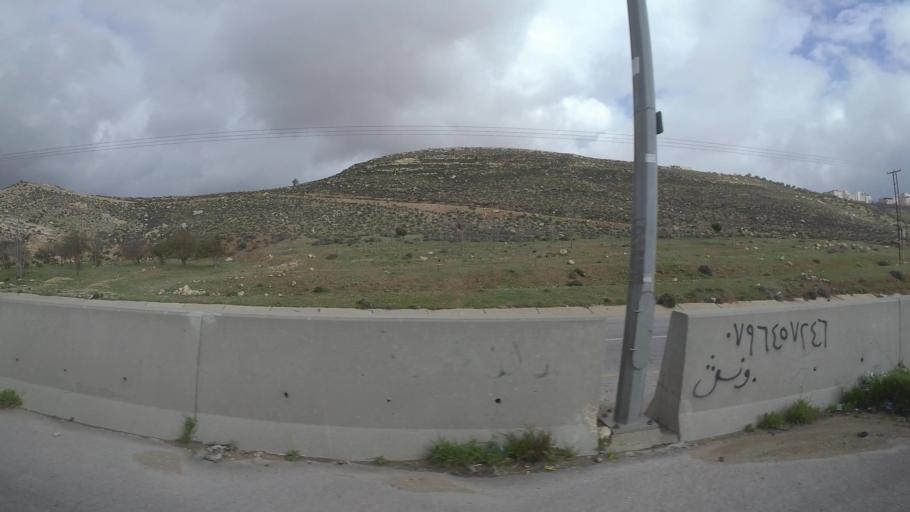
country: JO
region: Amman
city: Al Jubayhah
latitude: 32.0791
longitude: 35.8785
